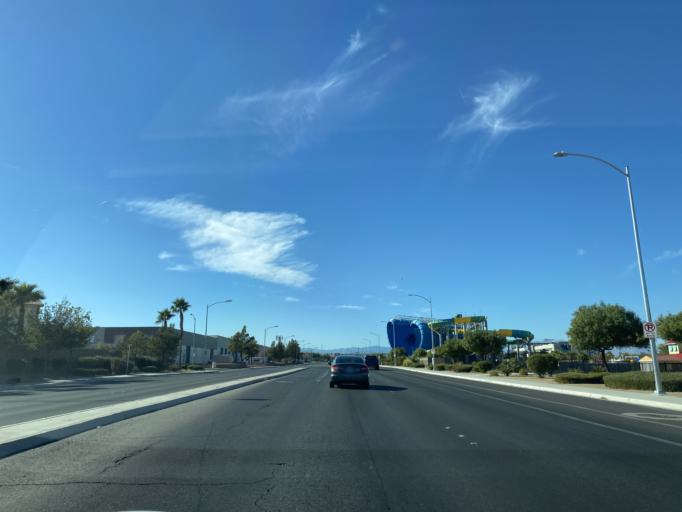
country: US
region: Nevada
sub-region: Clark County
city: Henderson
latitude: 36.0710
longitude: -115.0235
